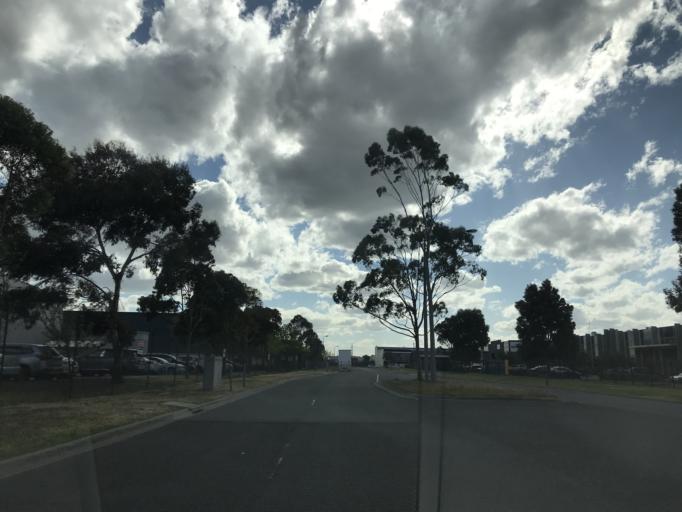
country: AU
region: Victoria
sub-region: Brimbank
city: Sunshine West
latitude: -37.8058
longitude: 144.8180
